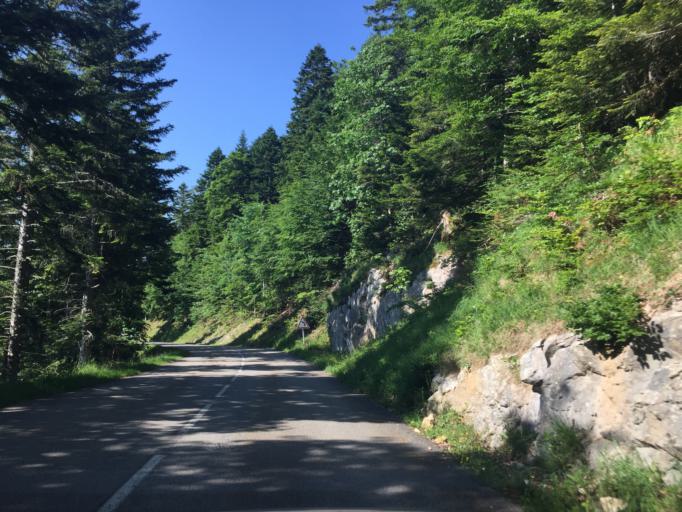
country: FR
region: Rhone-Alpes
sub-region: Departement de la Drome
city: Saint-Jean-en-Royans
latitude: 44.9316
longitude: 5.3233
